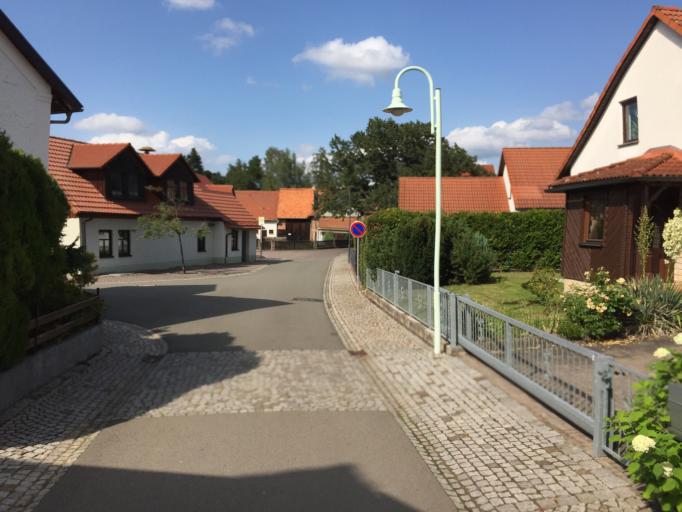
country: DE
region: Thuringia
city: Immelborn
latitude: 50.7843
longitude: 10.2704
